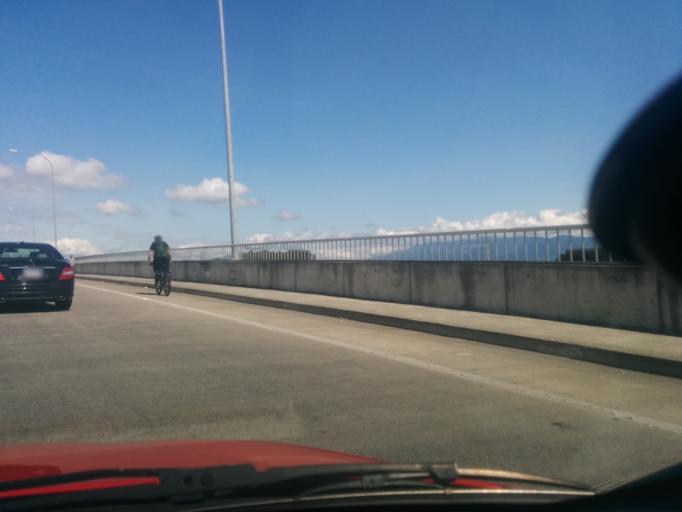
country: US
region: Washington
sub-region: Skagit County
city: Mount Vernon
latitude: 48.4438
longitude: -122.3353
